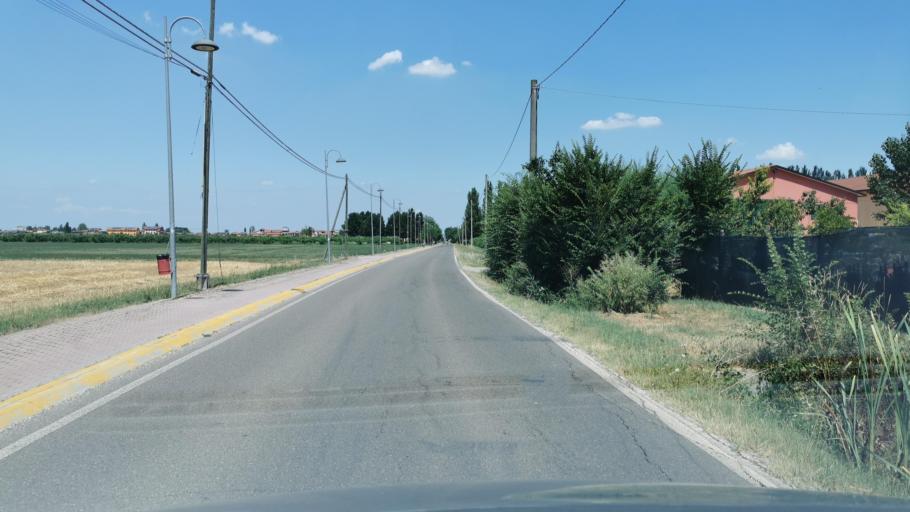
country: IT
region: Emilia-Romagna
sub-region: Provincia di Modena
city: Fossoli
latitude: 44.8097
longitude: 10.8896
